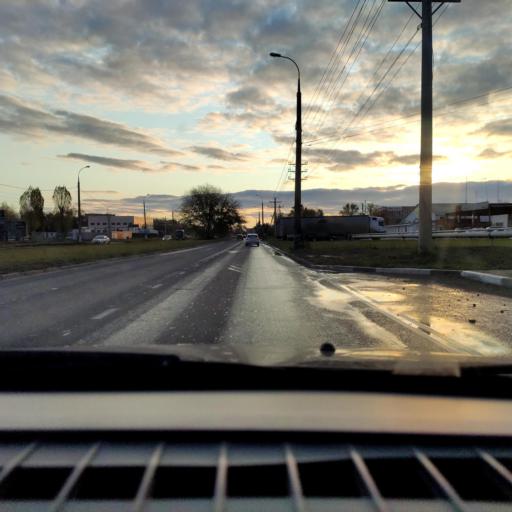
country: RU
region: Samara
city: Tol'yatti
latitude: 53.5589
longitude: 49.3124
